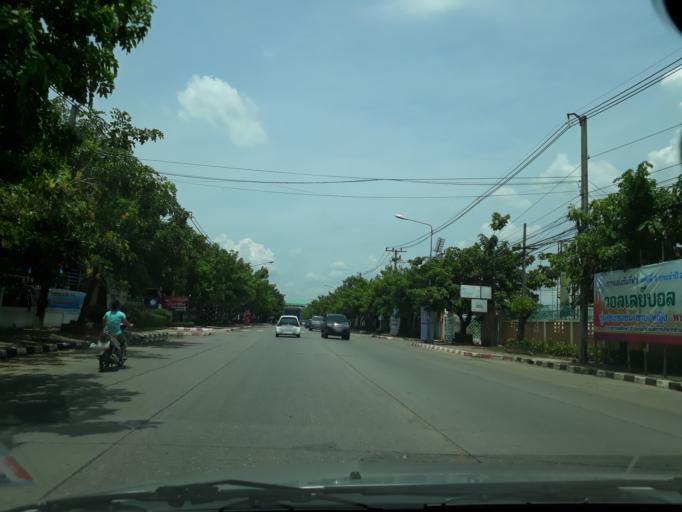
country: TH
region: Khon Kaen
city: Khon Kaen
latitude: 16.4145
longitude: 102.8265
